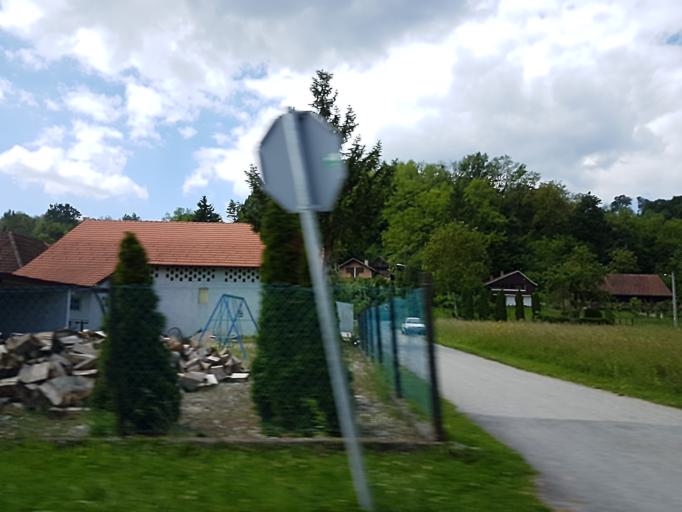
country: HR
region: Krapinsko-Zagorska
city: Zabok
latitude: 46.0538
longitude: 15.8024
